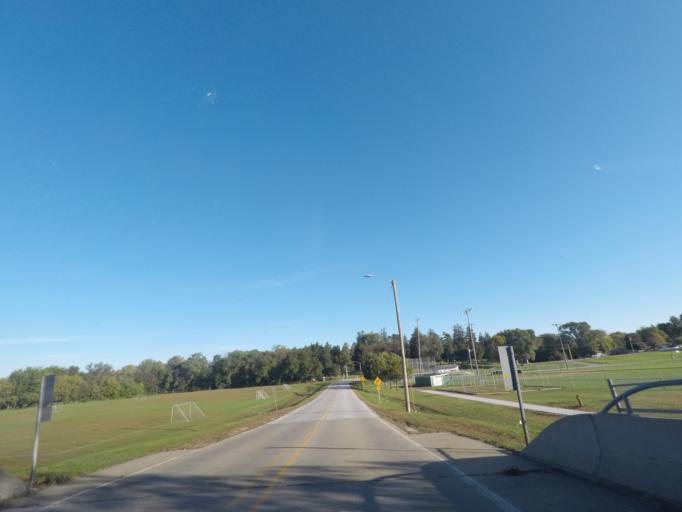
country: US
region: Iowa
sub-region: Story County
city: Nevada
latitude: 42.0177
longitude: -93.4629
